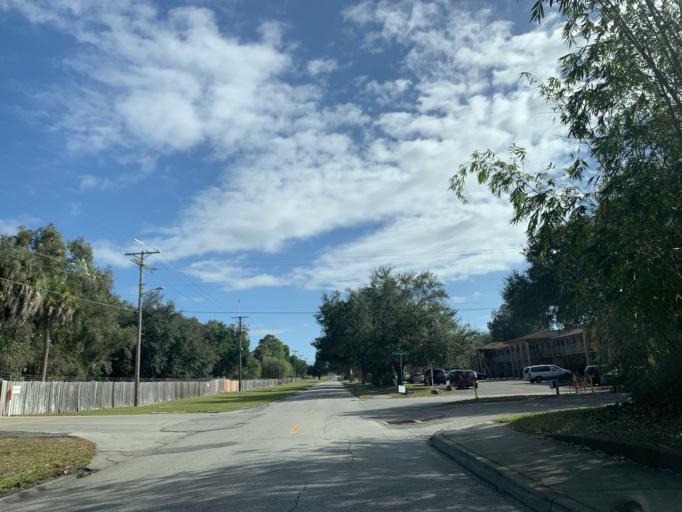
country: US
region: Florida
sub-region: Hillsborough County
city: Temple Terrace
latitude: 28.0399
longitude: -82.4153
